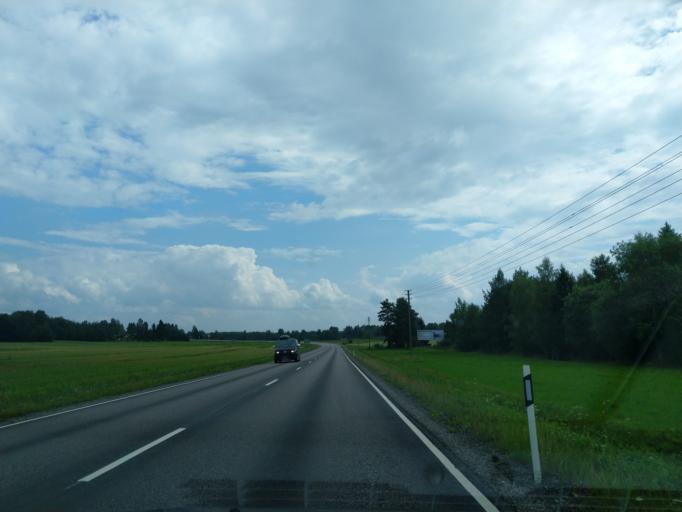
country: FI
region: South Karelia
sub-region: Imatra
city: Parikkala
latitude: 61.6074
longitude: 29.4604
